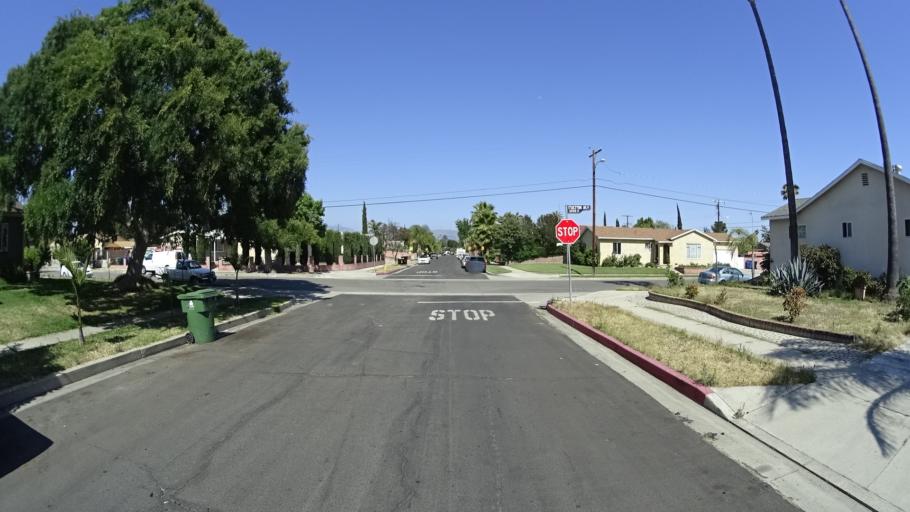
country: US
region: California
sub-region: Los Angeles County
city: Van Nuys
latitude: 34.2167
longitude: -118.4191
